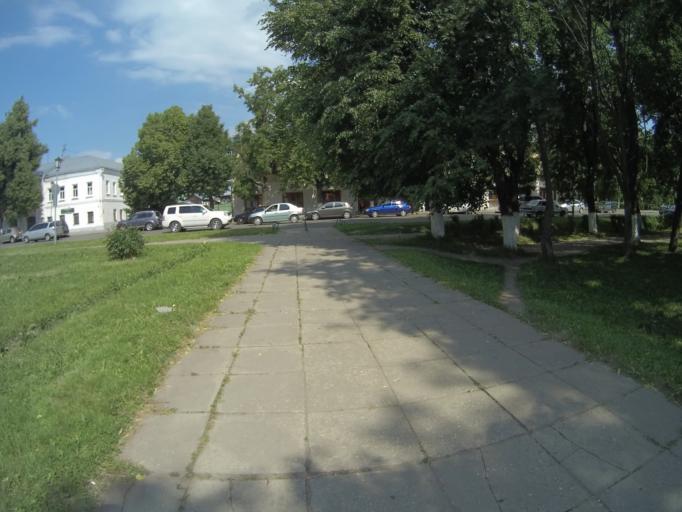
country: RU
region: Vladimir
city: Suzdal'
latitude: 56.4211
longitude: 40.4485
